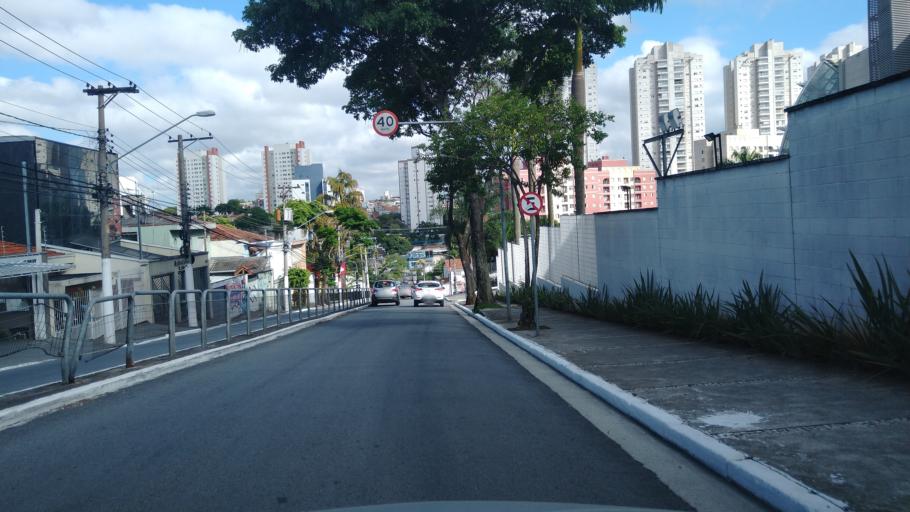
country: BR
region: Sao Paulo
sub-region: Sao Paulo
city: Sao Paulo
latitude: -23.4837
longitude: -46.6452
